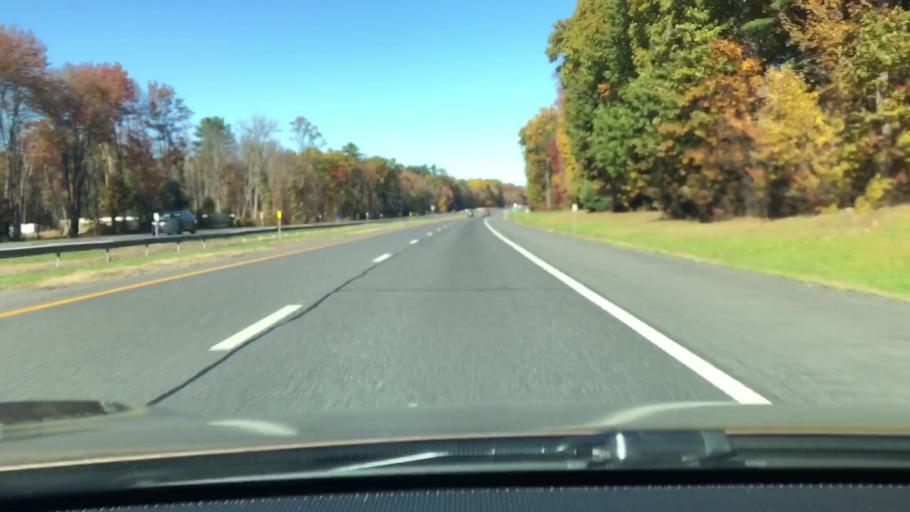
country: US
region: New York
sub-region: Ulster County
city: Tillson
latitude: 41.8200
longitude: -74.0567
